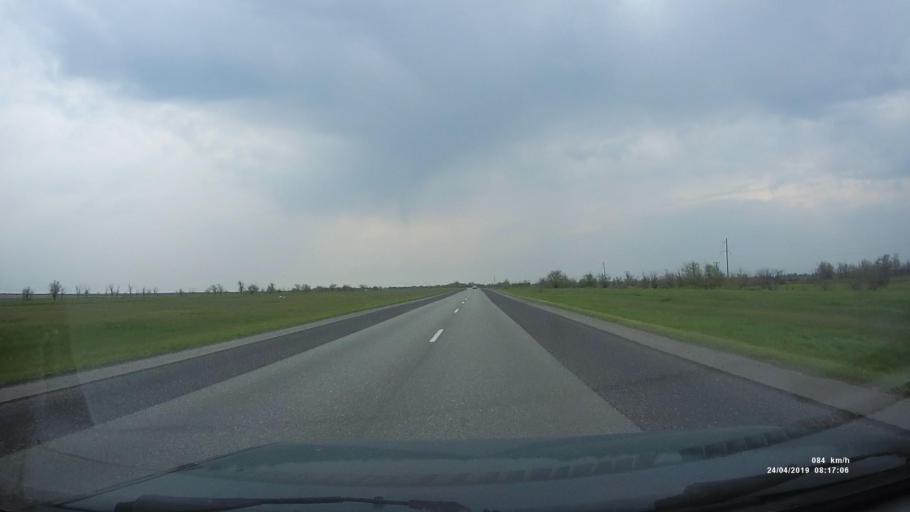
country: RU
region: Kalmykiya
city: Priyutnoye
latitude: 46.0982
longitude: 43.6238
